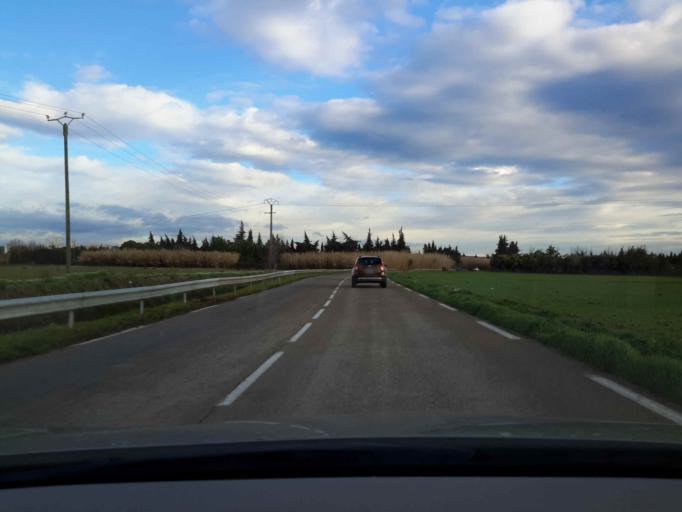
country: FR
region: Languedoc-Roussillon
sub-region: Departement du Gard
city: Caissargues
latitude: 43.7997
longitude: 4.3535
